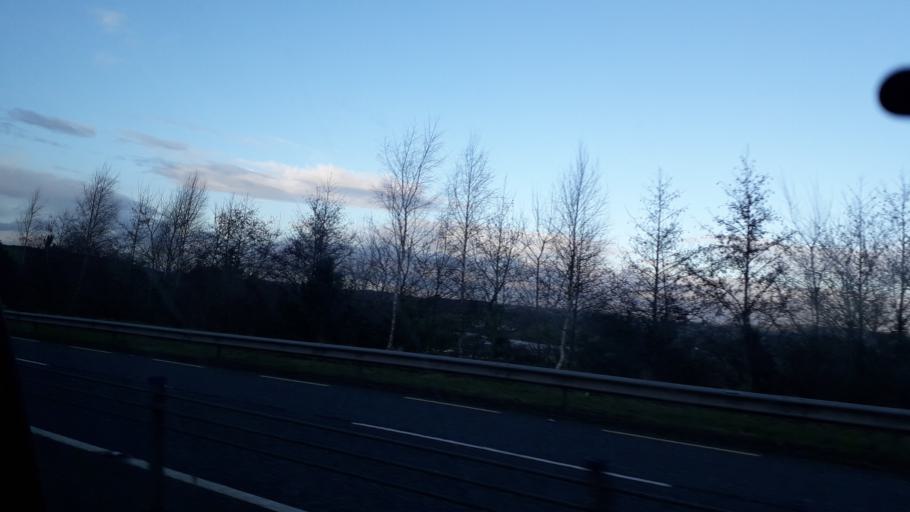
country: IE
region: Ulster
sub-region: County Monaghan
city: Castleblayney
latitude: 54.1216
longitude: -6.7643
